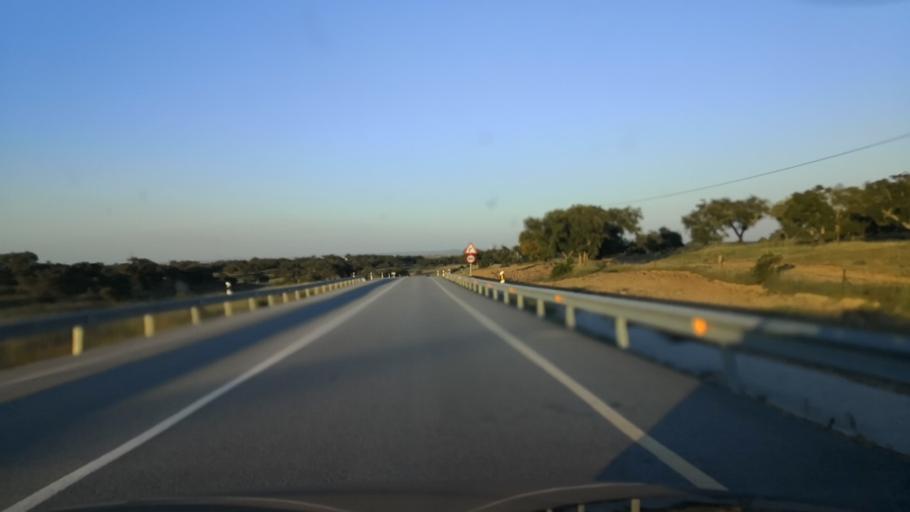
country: ES
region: Extremadura
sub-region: Provincia de Caceres
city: Salorino
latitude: 39.5102
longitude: -7.1107
